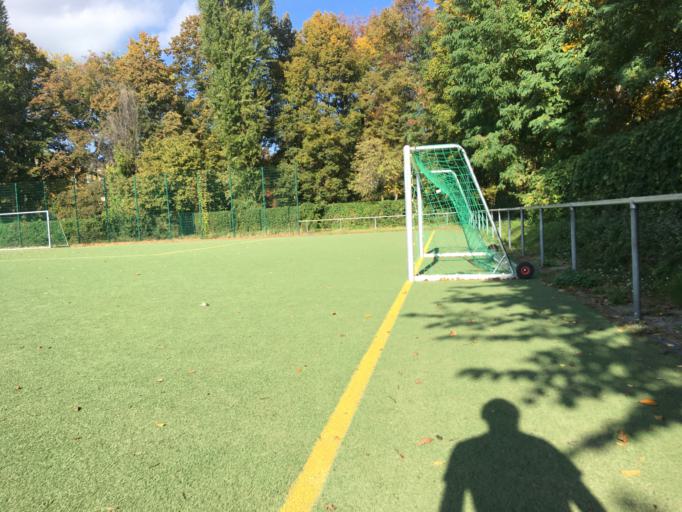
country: DE
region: Berlin
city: Wedding Bezirk
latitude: 52.5646
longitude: 13.3574
